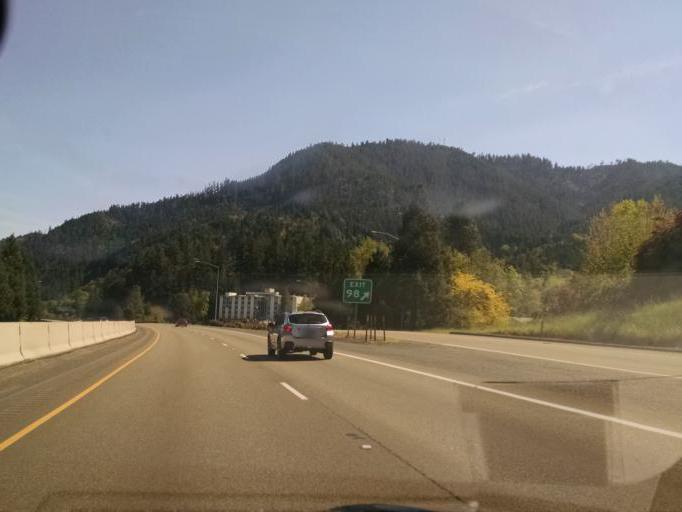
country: US
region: Oregon
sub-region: Douglas County
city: Canyonville
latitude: 42.9298
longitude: -123.2828
